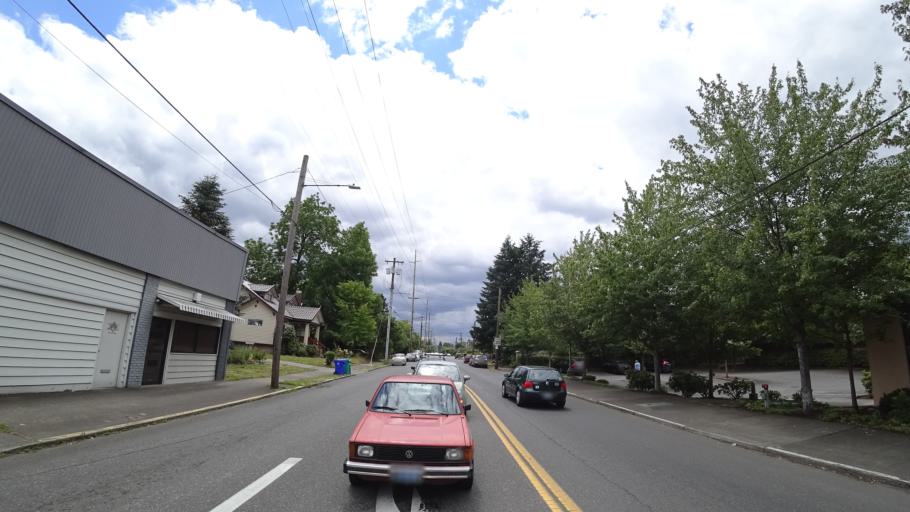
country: US
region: Oregon
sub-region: Multnomah County
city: Portland
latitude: 45.5697
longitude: -122.6956
